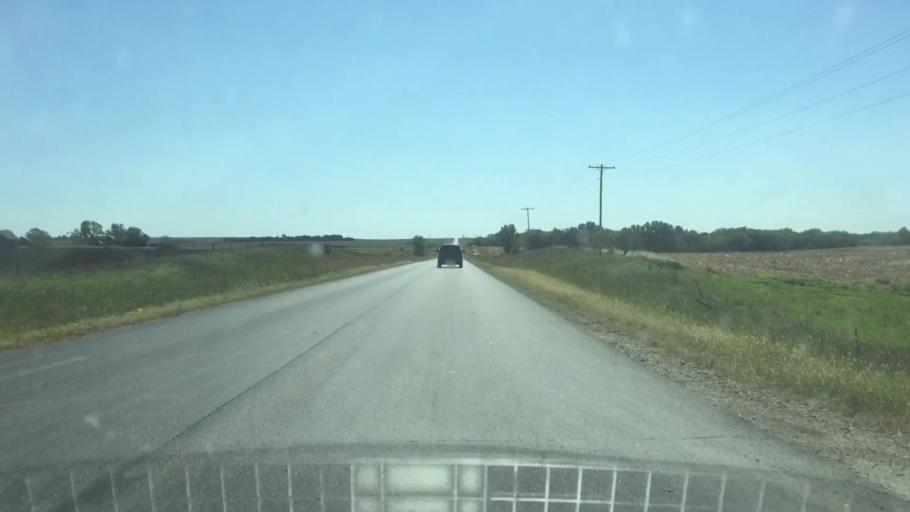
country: US
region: Kansas
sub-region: Marshall County
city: Marysville
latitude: 39.8849
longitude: -96.6013
